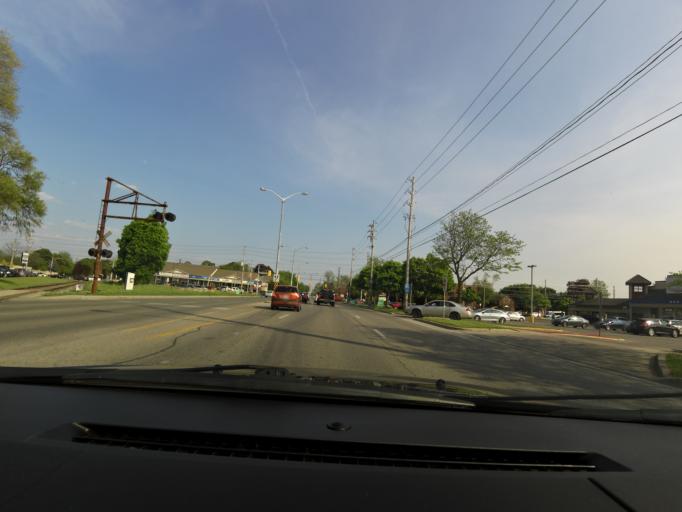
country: CA
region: Ontario
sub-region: Wellington County
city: Guelph
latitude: 43.5591
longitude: -80.2693
